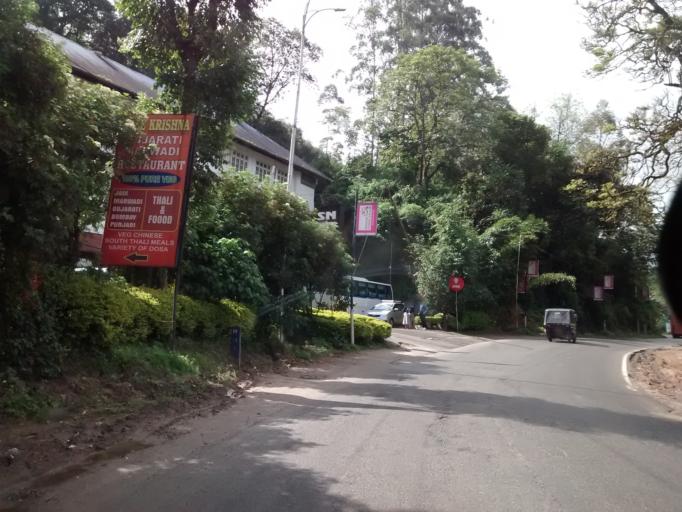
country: IN
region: Kerala
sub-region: Idukki
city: Munnar
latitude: 10.0812
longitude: 77.0619
